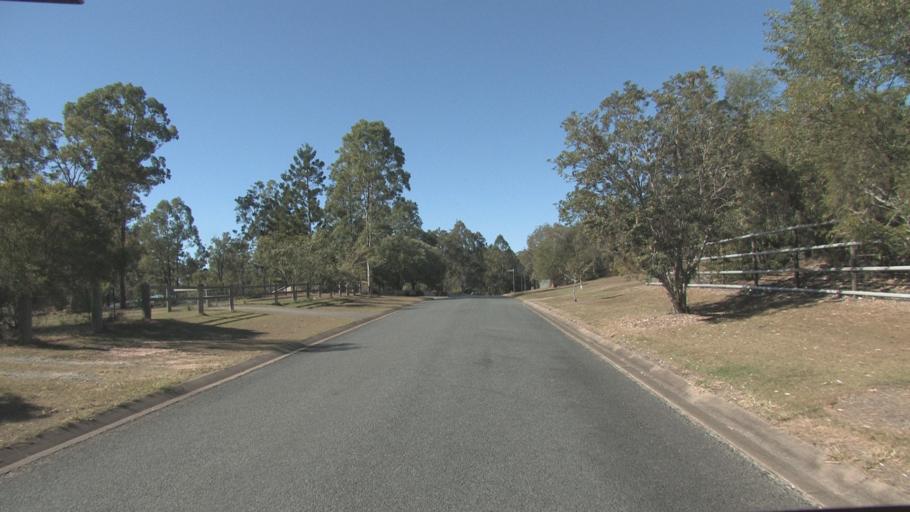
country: AU
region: Queensland
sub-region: Logan
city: North Maclean
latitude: -27.8194
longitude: 152.9506
